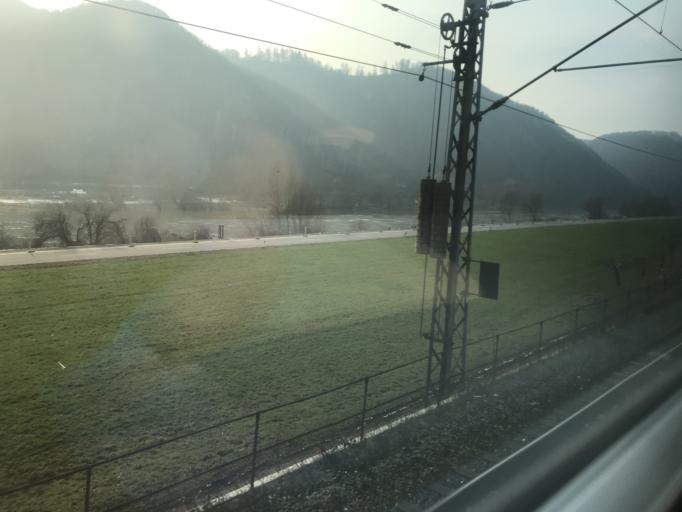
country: DE
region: Rheinland-Pfalz
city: Moselkern
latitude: 50.1871
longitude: 7.3596
